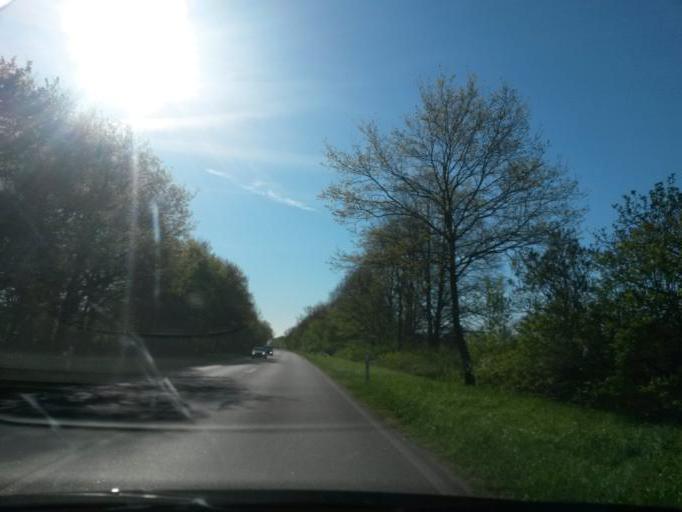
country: DE
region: Schleswig-Holstein
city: Rellingen
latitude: 53.6134
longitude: 9.7976
